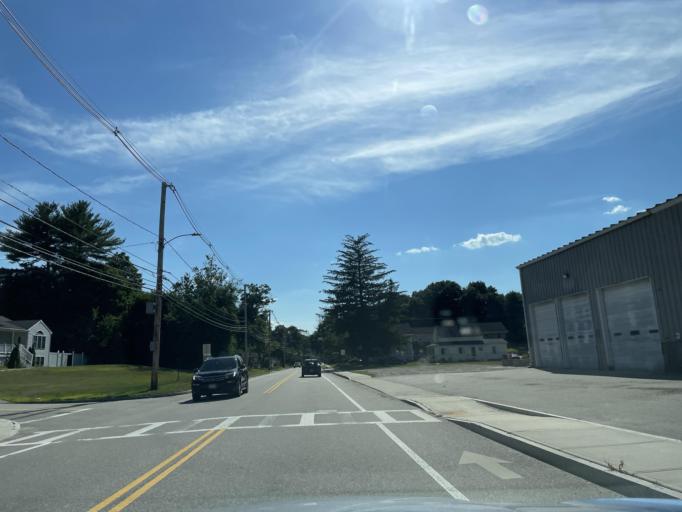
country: US
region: Massachusetts
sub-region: Worcester County
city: Oxford
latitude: 42.1156
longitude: -71.8693
